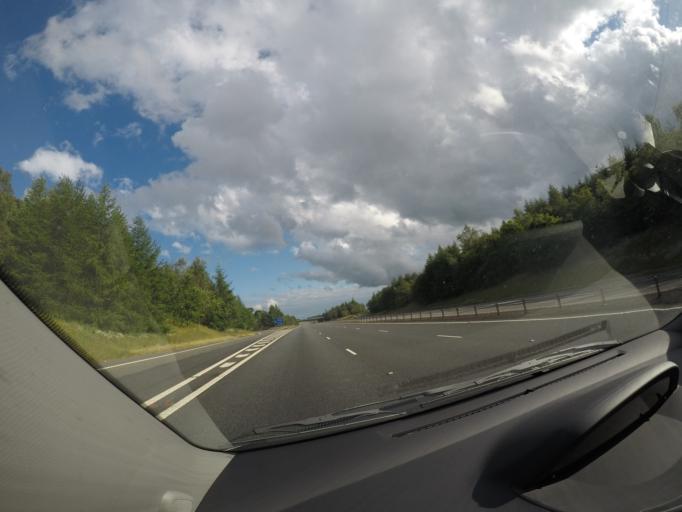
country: GB
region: Scotland
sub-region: Dumfries and Galloway
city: Lockerbie
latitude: 55.1367
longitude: -3.3703
